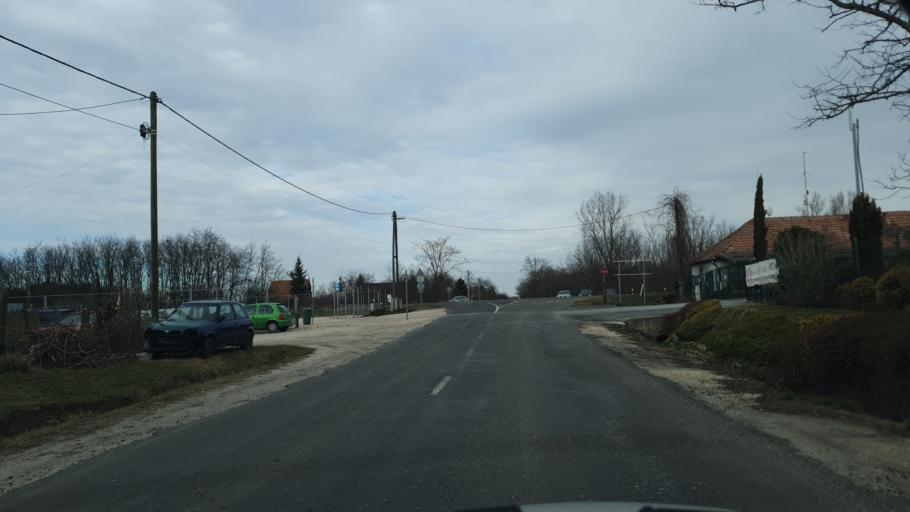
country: HU
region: Pest
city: Albertirsa
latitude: 47.2615
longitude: 19.6081
